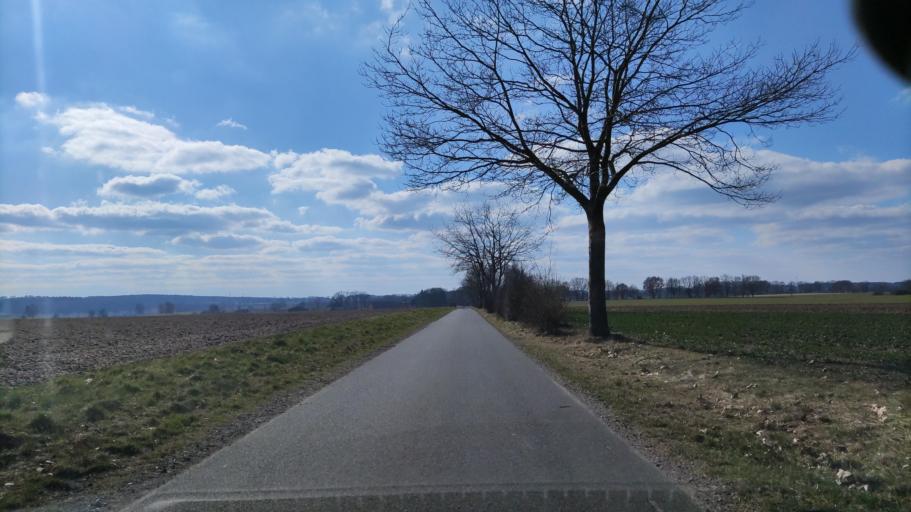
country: DE
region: Lower Saxony
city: Jelmstorf
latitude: 53.0966
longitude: 10.5134
